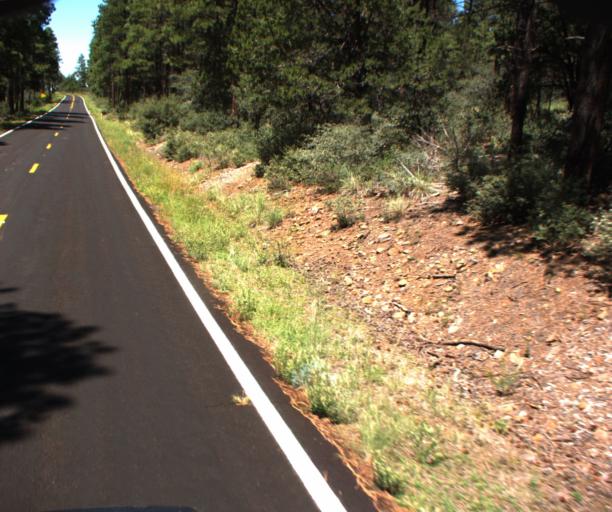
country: US
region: Arizona
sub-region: Greenlee County
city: Morenci
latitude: 33.4839
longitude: -109.3700
